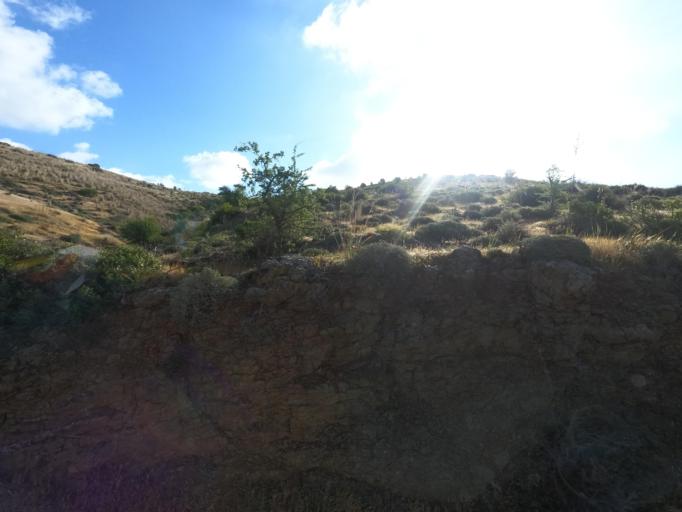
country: CY
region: Lefkosia
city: Peristerona
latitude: 35.0668
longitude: 33.0482
